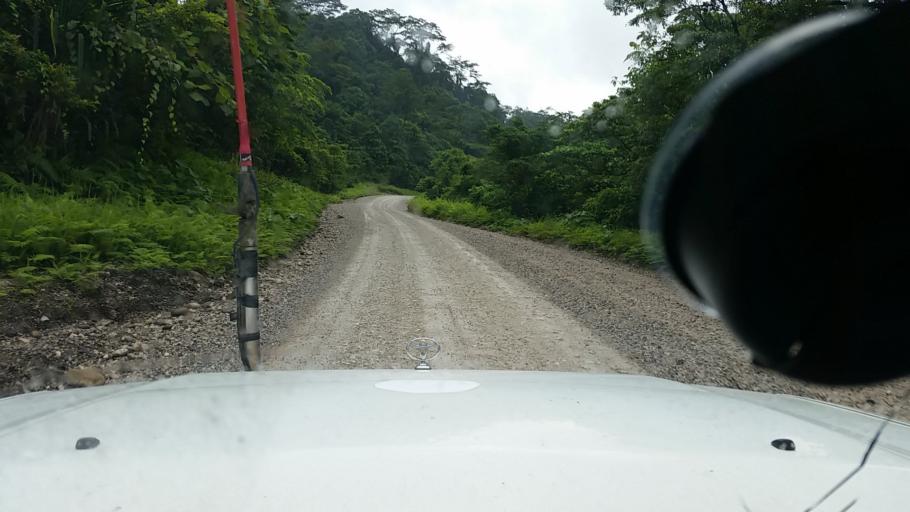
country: PG
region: Western Province
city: Kiunga
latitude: -5.6071
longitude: 141.2282
